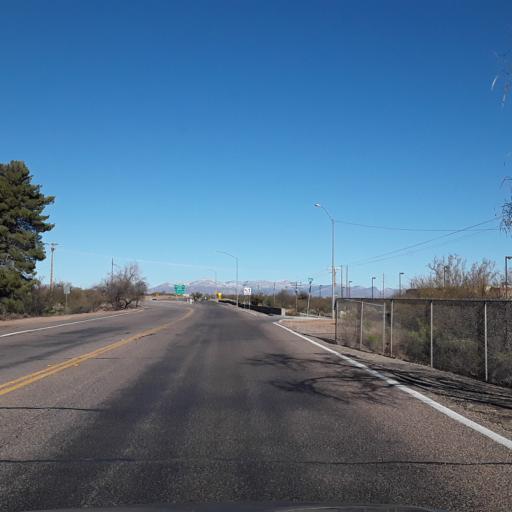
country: US
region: Arizona
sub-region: Cochise County
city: Sierra Vista
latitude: 31.5591
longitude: -110.3073
